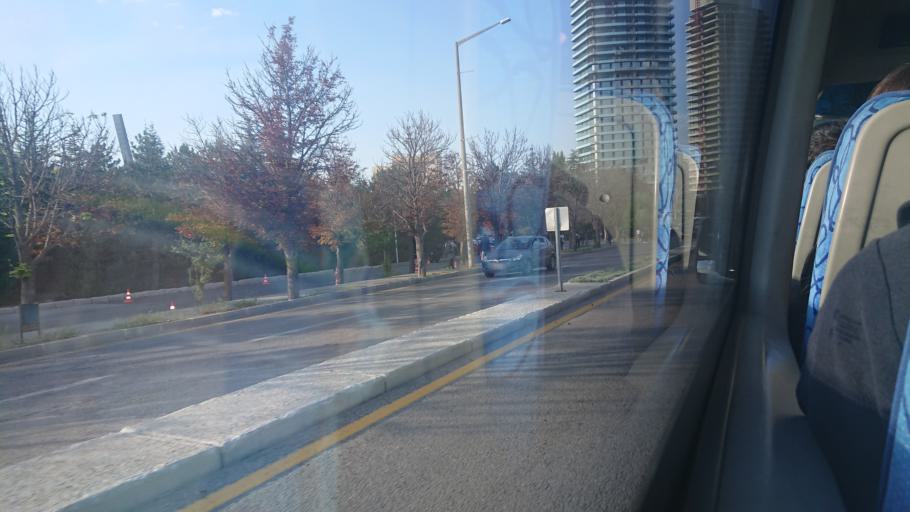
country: TR
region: Ankara
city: Ankara
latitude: 39.9065
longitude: 32.7839
